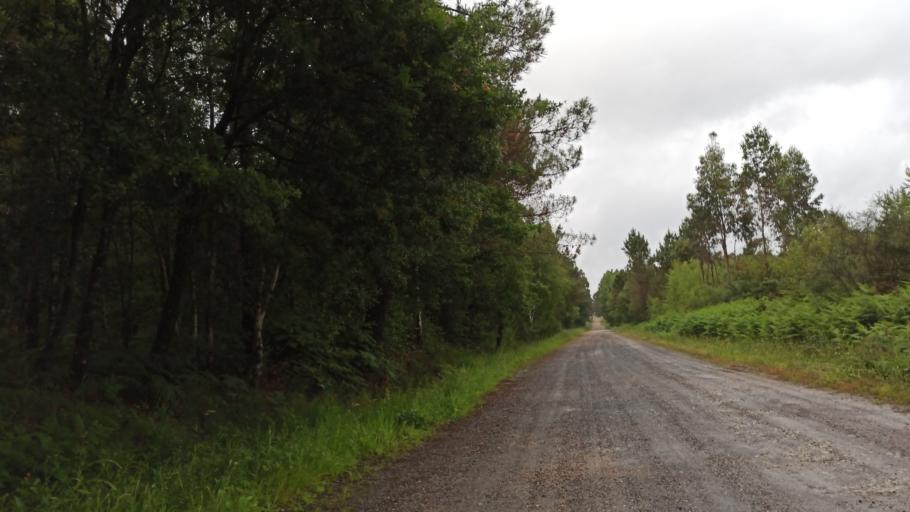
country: ES
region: Galicia
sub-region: Provincia da Coruna
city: Santiso
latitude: 42.7630
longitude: -8.0272
